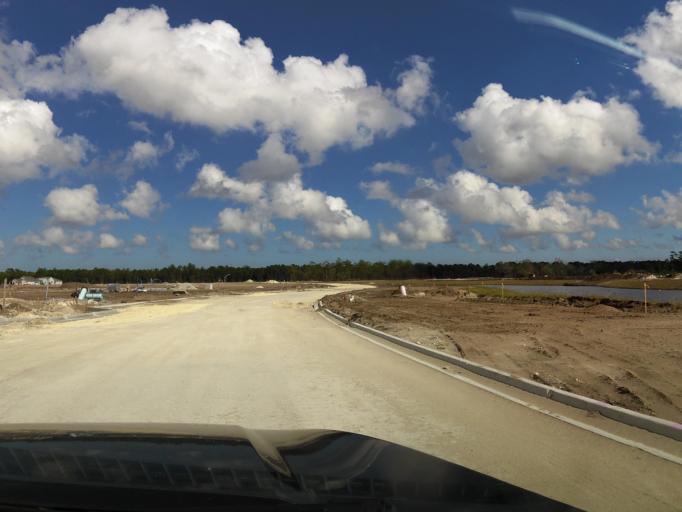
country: US
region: Florida
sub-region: Saint Johns County
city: Ponte Vedra Beach
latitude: 30.2434
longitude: -81.4949
